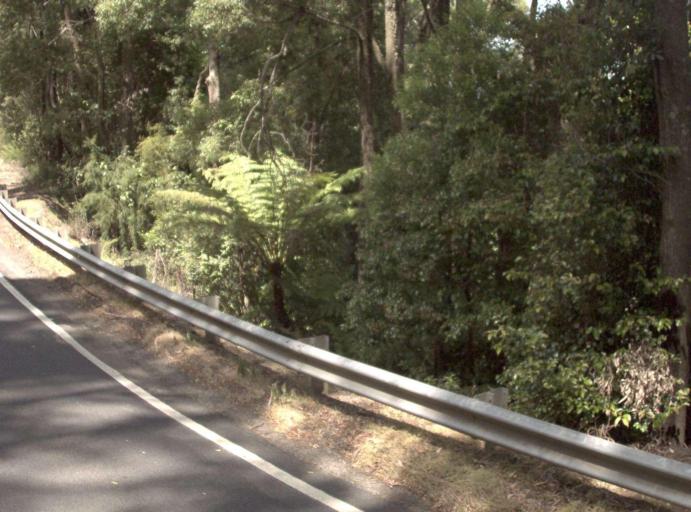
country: AU
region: New South Wales
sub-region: Bombala
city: Bombala
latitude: -37.5560
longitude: 149.3543
